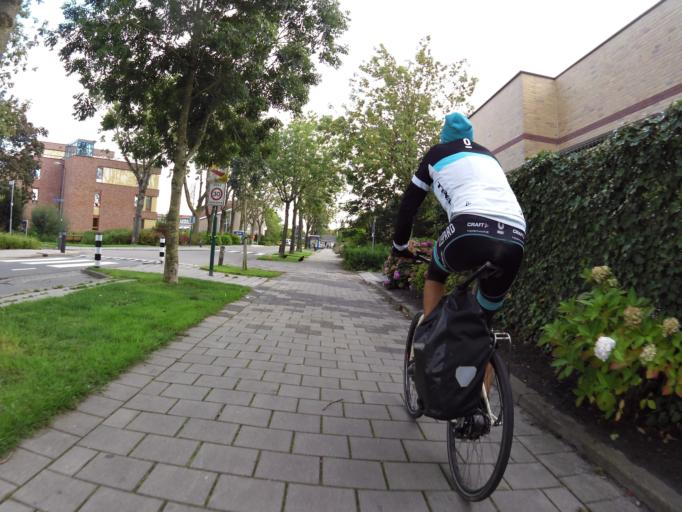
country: NL
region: Utrecht
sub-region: Stichtse Vecht
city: Breukelen
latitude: 52.1488
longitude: 4.9493
